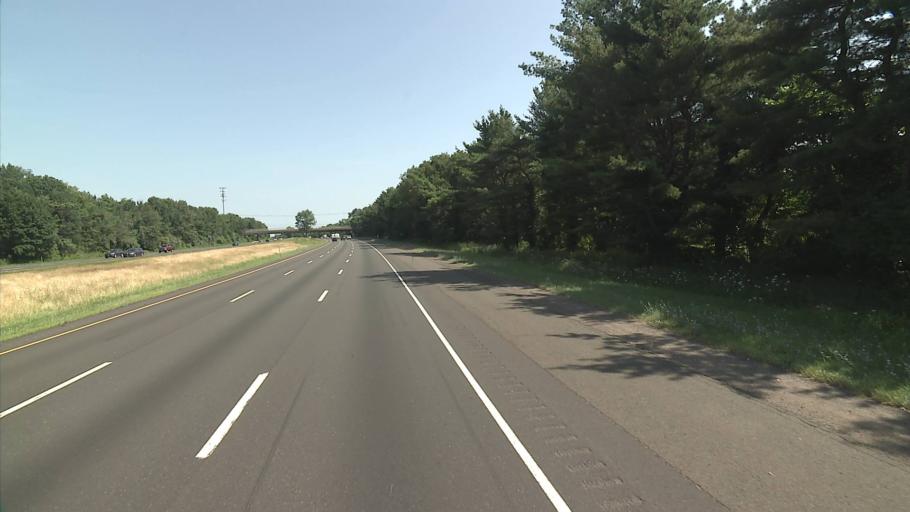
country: US
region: Connecticut
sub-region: New Haven County
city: Wallingford
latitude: 41.4854
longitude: -72.7677
